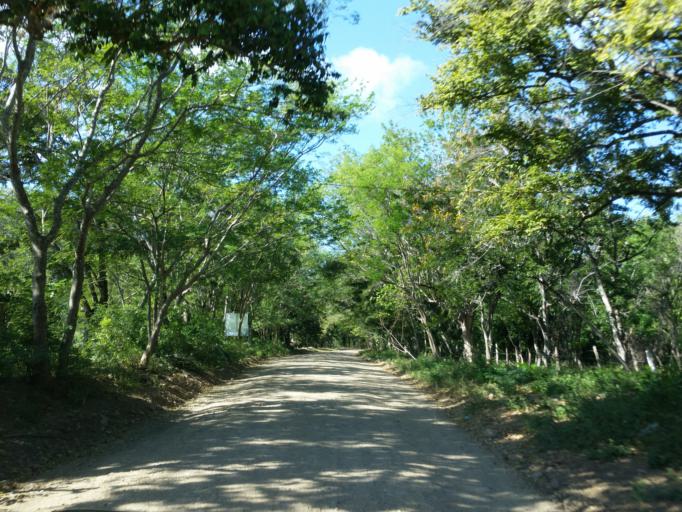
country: NI
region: Rivas
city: San Juan del Sur
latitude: 11.2067
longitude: -85.8053
